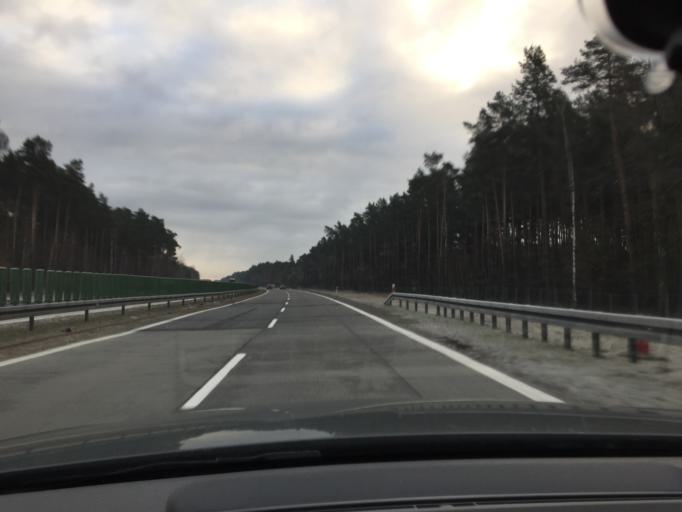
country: PL
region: Lubusz
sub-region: Powiat zarski
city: Lipinki Luzyckie
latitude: 51.6144
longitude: 14.9268
